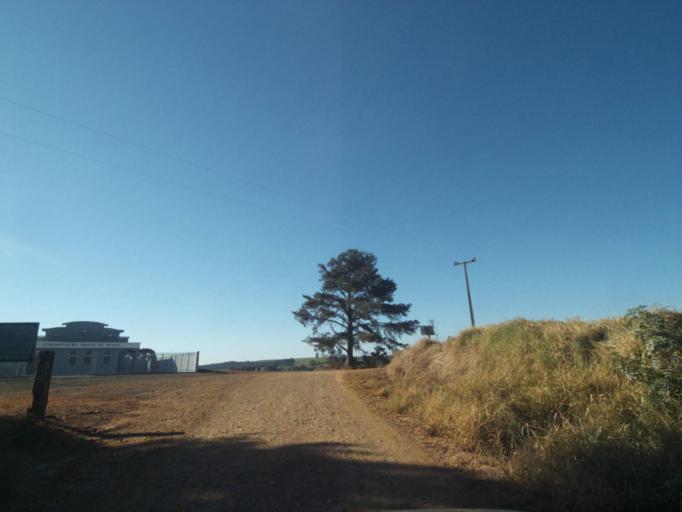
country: BR
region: Parana
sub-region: Tibagi
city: Tibagi
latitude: -24.5430
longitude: -50.5073
